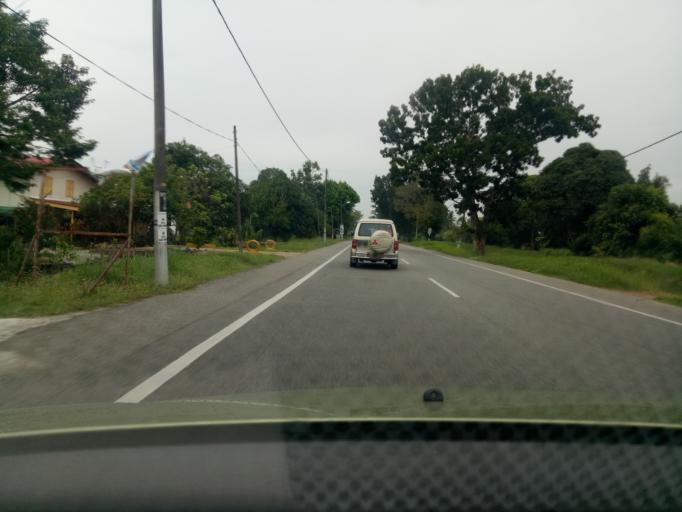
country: MY
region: Kedah
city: Gurun
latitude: 5.8899
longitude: 100.4418
